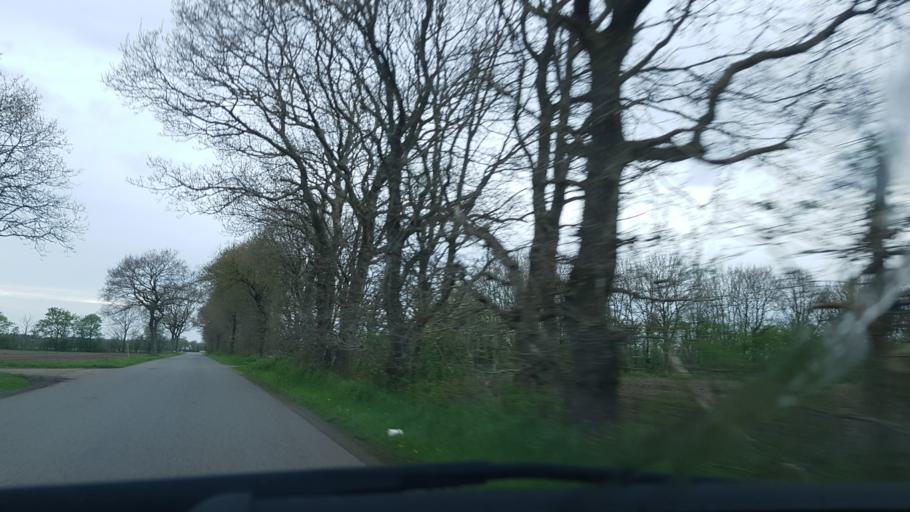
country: DK
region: South Denmark
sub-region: Vejen Kommune
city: Vejen
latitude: 55.4577
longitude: 9.1693
